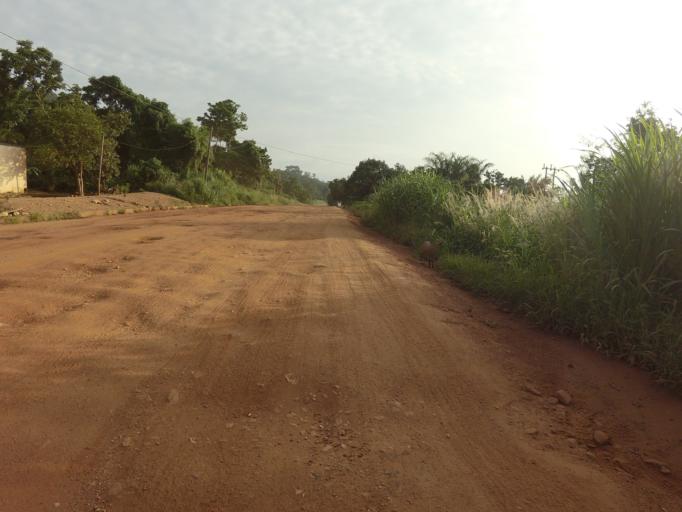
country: TG
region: Plateaux
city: Kpalime
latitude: 6.9172
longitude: 0.4582
